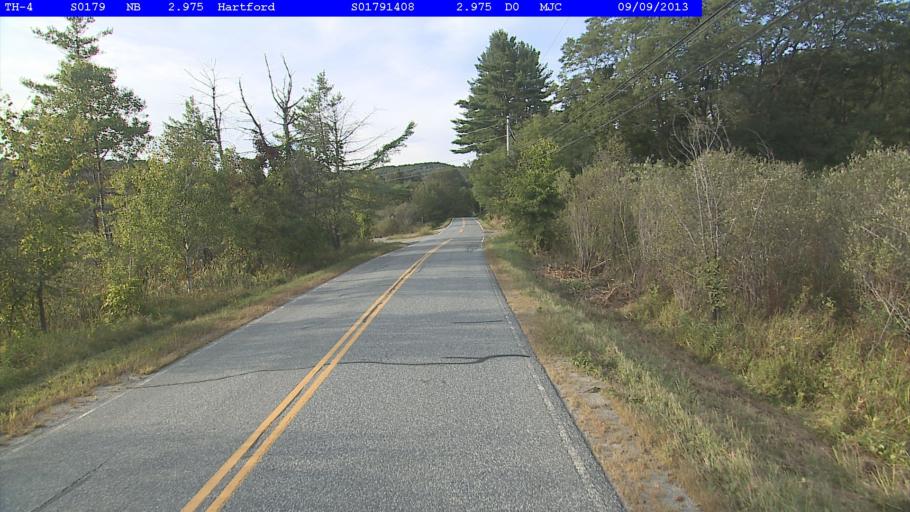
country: US
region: Vermont
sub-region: Windsor County
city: Woodstock
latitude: 43.6835
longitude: -72.4445
